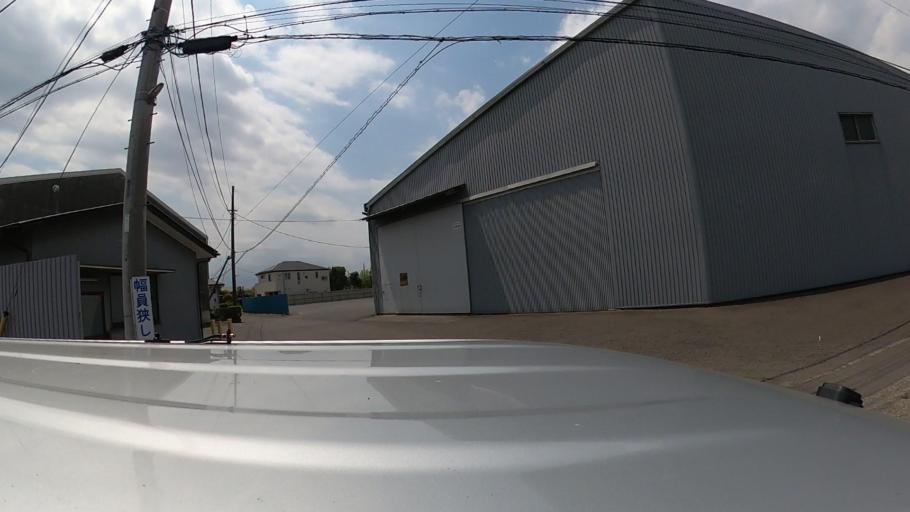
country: JP
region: Kanagawa
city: Chigasaki
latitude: 35.3865
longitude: 139.4020
